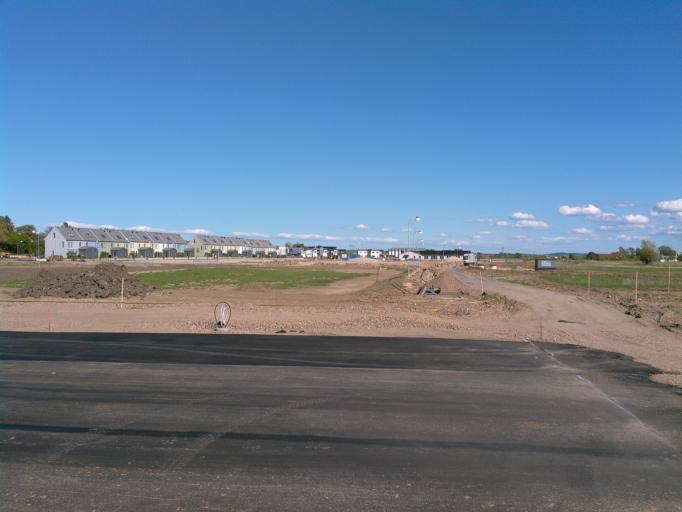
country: SE
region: Skane
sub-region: Lunds Kommun
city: Lund
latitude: 55.6903
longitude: 13.2281
